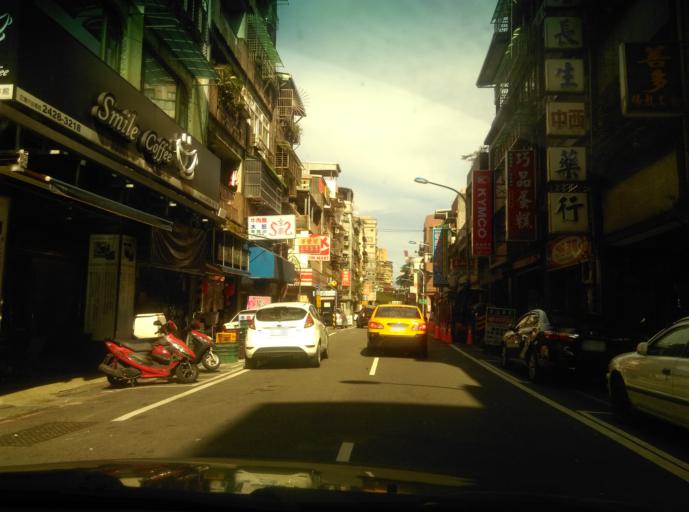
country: TW
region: Taiwan
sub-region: Keelung
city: Keelung
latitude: 25.1344
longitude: 121.7477
